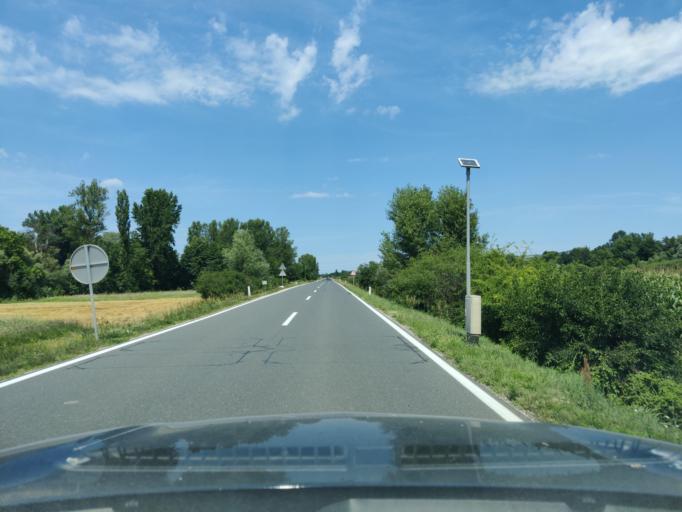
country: SI
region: Lendava-Lendva
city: Lendava
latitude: 46.5234
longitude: 16.4417
